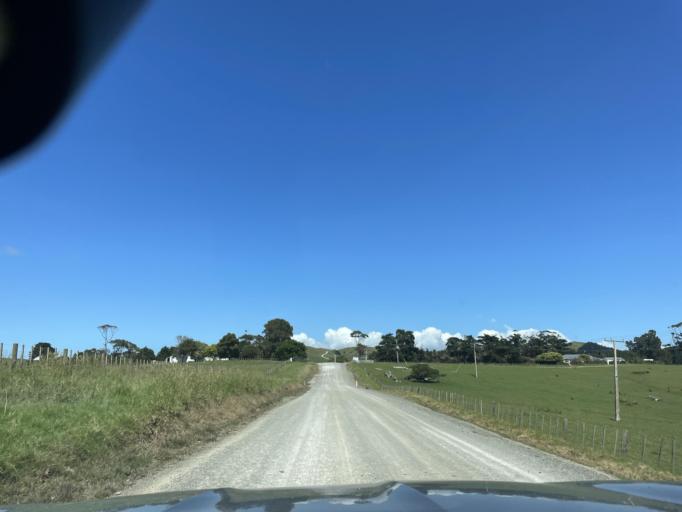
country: NZ
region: Auckland
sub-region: Auckland
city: Wellsford
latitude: -36.2873
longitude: 174.3397
